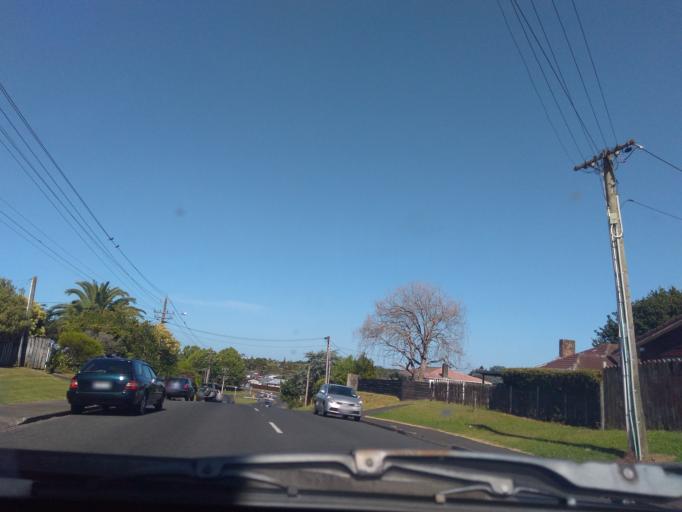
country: NZ
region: Auckland
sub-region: Auckland
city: Rosebank
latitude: -36.8585
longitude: 174.6072
